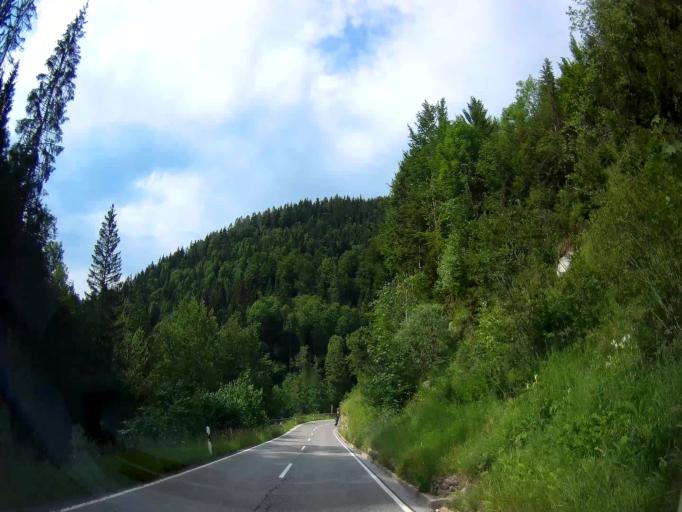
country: DE
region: Bavaria
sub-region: Upper Bavaria
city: Berchtesgaden
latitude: 47.6321
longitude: 13.0588
